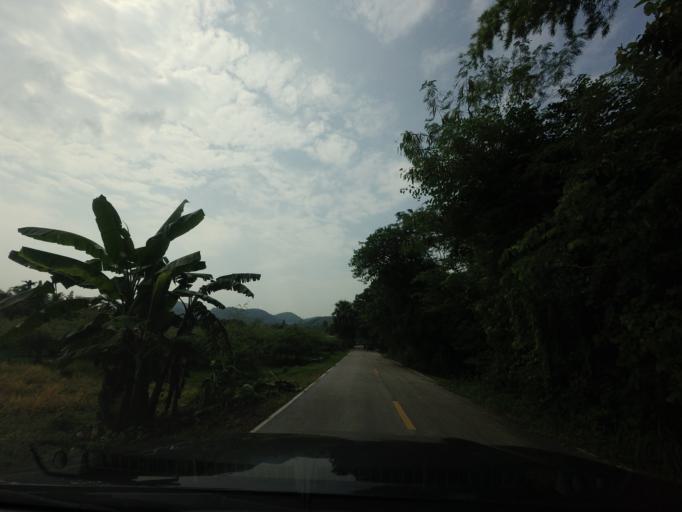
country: TH
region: Loei
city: Chiang Khan
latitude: 17.8152
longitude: 101.5549
